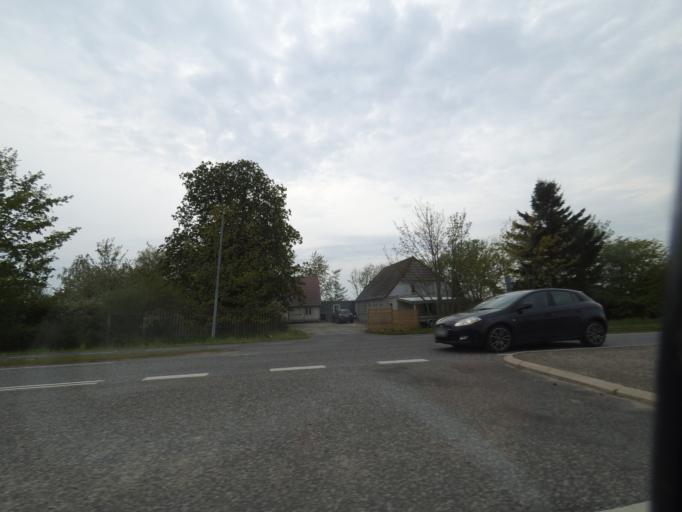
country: DK
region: South Denmark
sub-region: Faaborg-Midtfyn Kommune
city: Arslev
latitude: 55.3042
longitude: 10.4523
